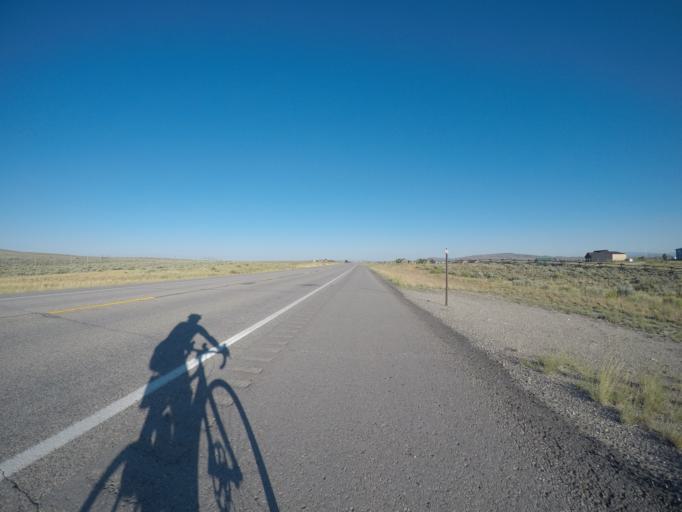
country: US
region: Wyoming
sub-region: Sublette County
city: Pinedale
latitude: 42.8769
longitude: -109.9546
